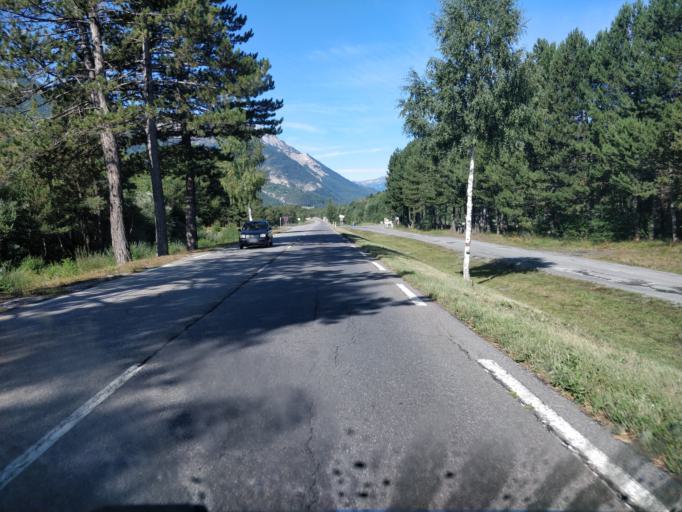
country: FR
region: Provence-Alpes-Cote d'Azur
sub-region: Departement des Alpes-de-Haute-Provence
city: Barcelonnette
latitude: 44.3863
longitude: 6.6216
